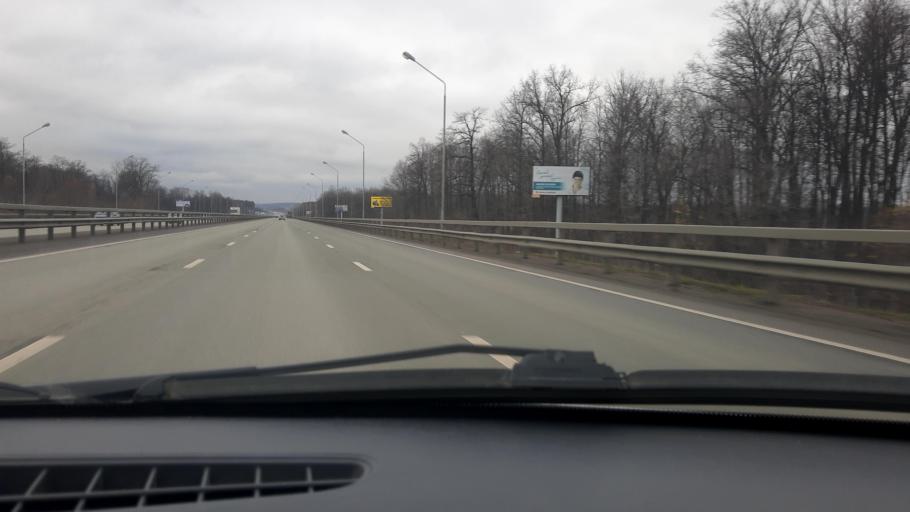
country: RU
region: Bashkortostan
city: Ufa
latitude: 54.6659
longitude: 55.8553
